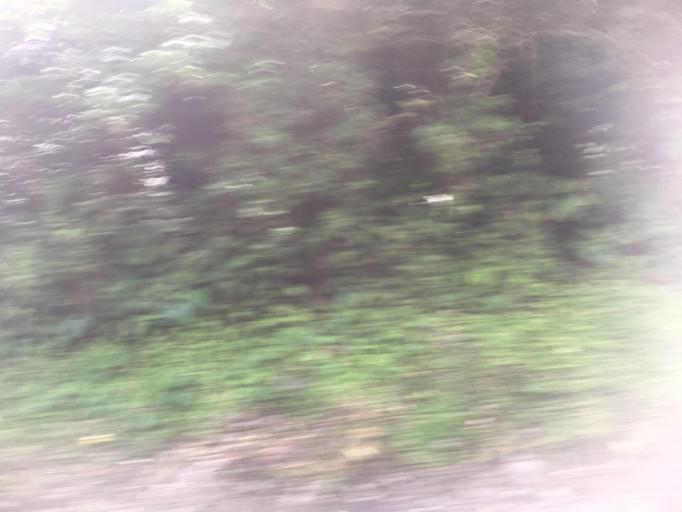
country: TW
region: Taiwan
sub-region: Yilan
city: Yilan
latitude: 24.5548
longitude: 121.4648
